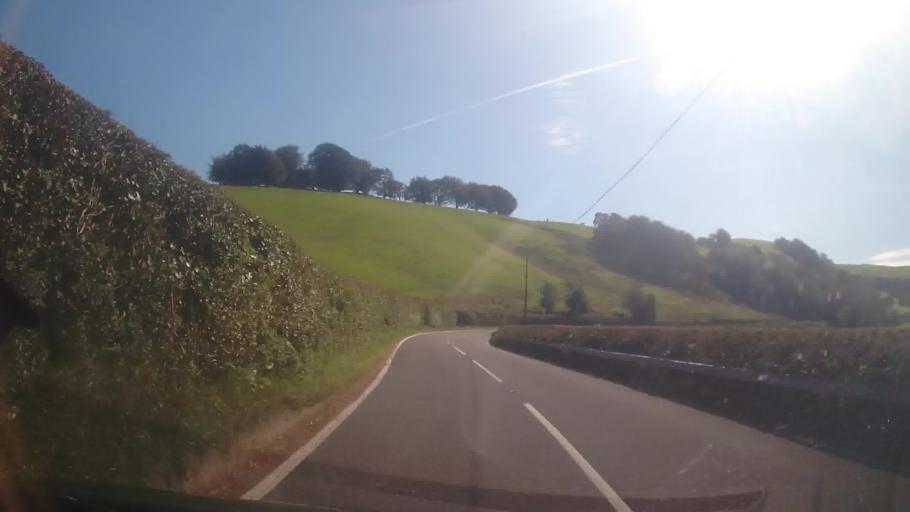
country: GB
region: Wales
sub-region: Sir Powys
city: Mochdre
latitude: 52.4714
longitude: -3.3194
